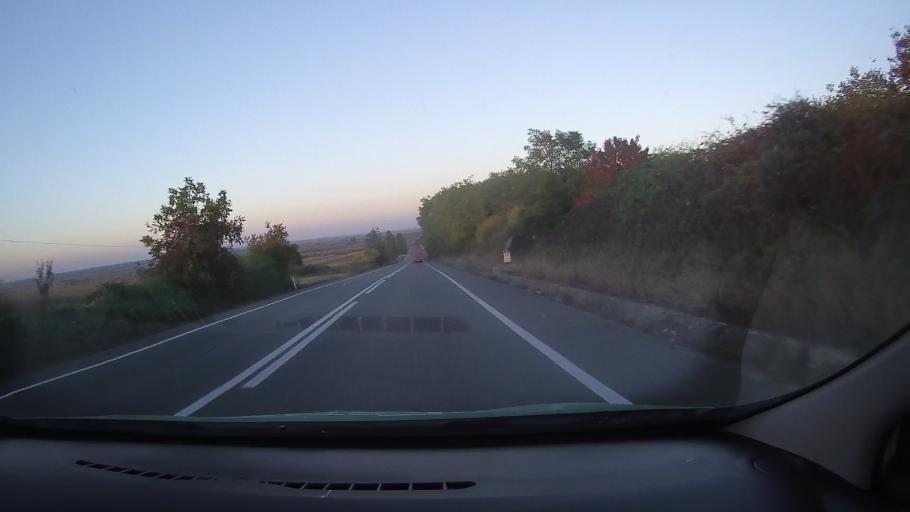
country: RO
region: Bihor
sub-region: Comuna Cherechiu
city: Cherechiu
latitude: 47.3790
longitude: 22.1398
